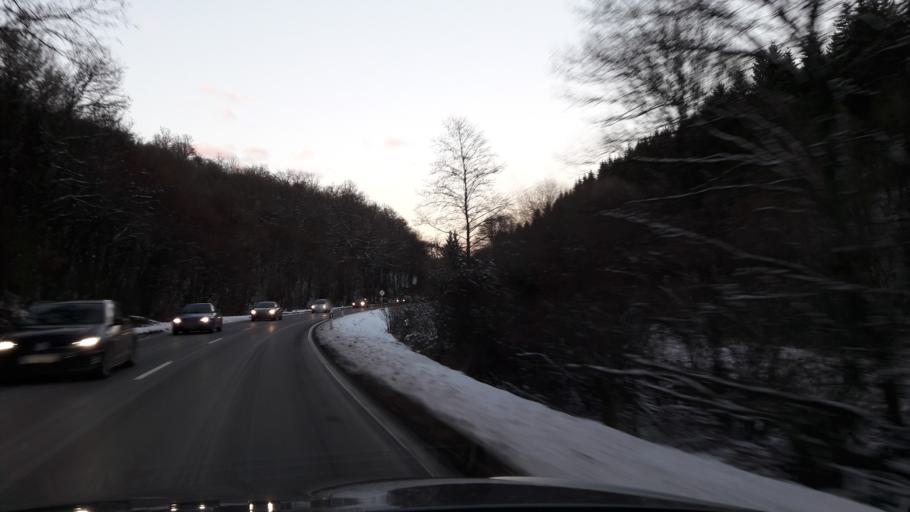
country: DE
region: Rheinland-Pfalz
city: Ruschberg
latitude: 49.6270
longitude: 7.2814
